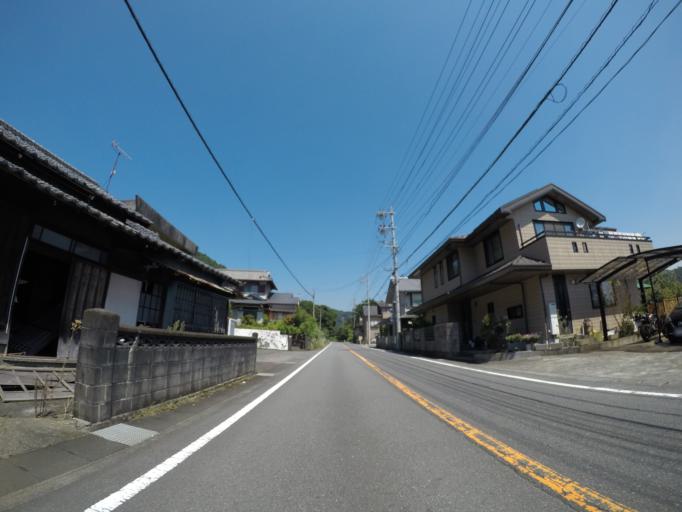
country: JP
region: Shizuoka
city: Fujinomiya
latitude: 35.1739
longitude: 138.6156
